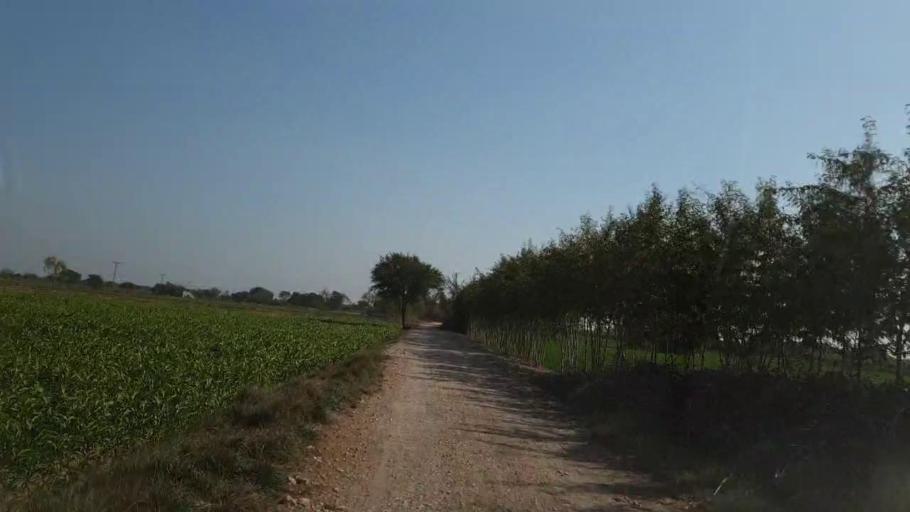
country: PK
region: Sindh
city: Matiari
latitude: 25.5043
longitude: 68.4763
